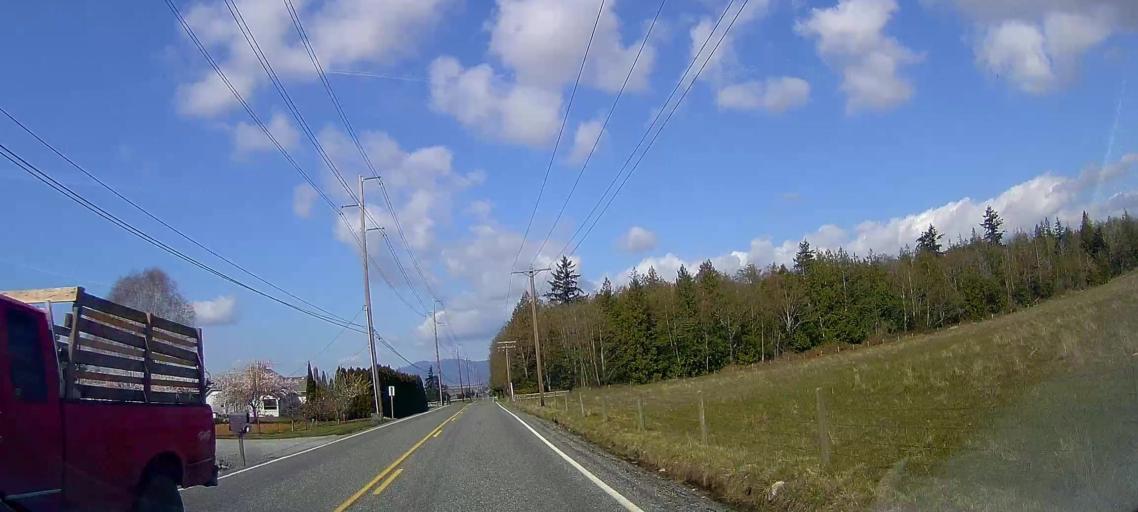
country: US
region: Washington
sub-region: Skagit County
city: Burlington
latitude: 48.5000
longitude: -122.4445
